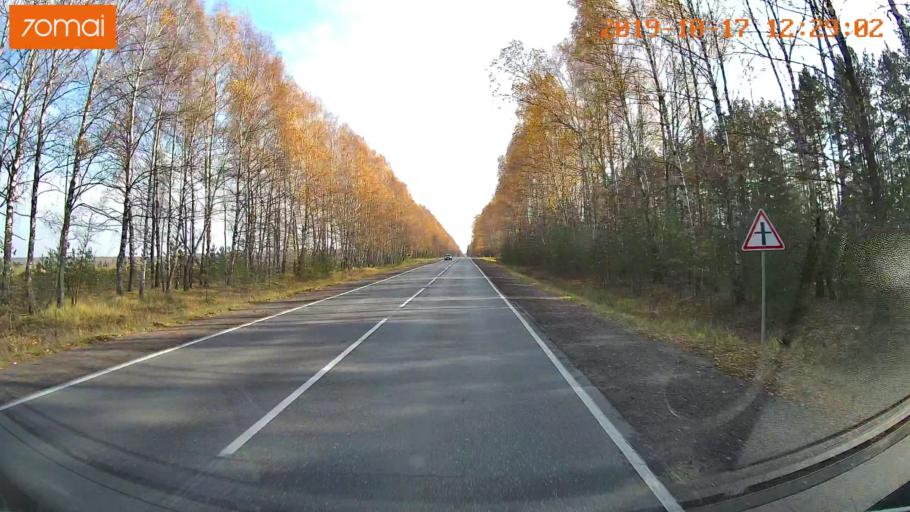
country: RU
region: Rjazan
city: Syntul
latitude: 54.9845
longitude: 41.2825
